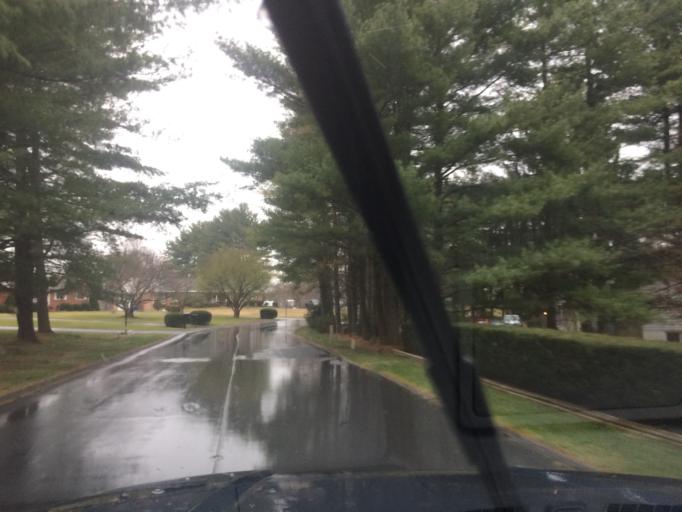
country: US
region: Maryland
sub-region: Carroll County
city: Eldersburg
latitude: 39.3738
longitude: -76.9140
